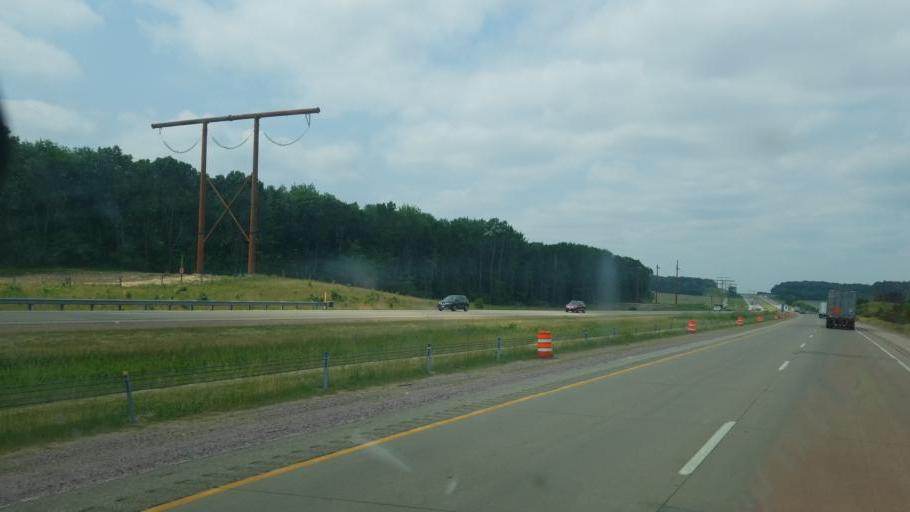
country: US
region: Wisconsin
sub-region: Sauk County
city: Baraboo
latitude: 43.5483
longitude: -89.6485
